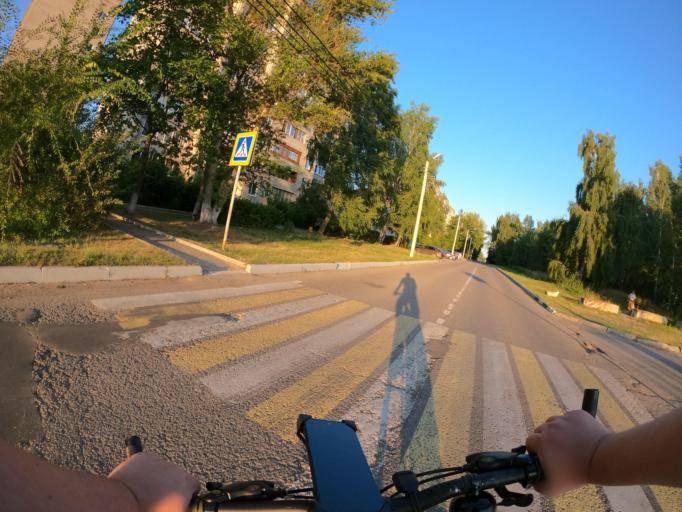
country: RU
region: Moskovskaya
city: Beloozerskiy
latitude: 55.4616
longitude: 38.4332
